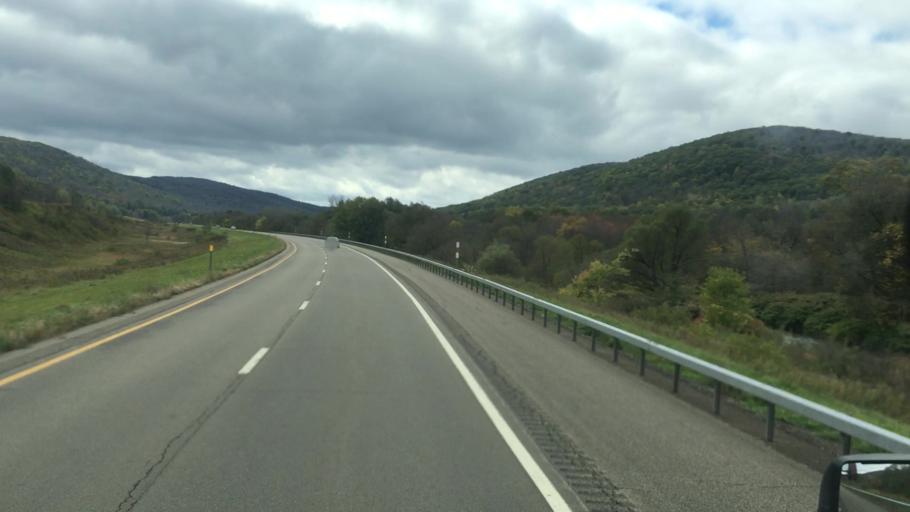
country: US
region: New York
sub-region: Allegany County
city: Cuba
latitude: 42.2100
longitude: -78.3244
